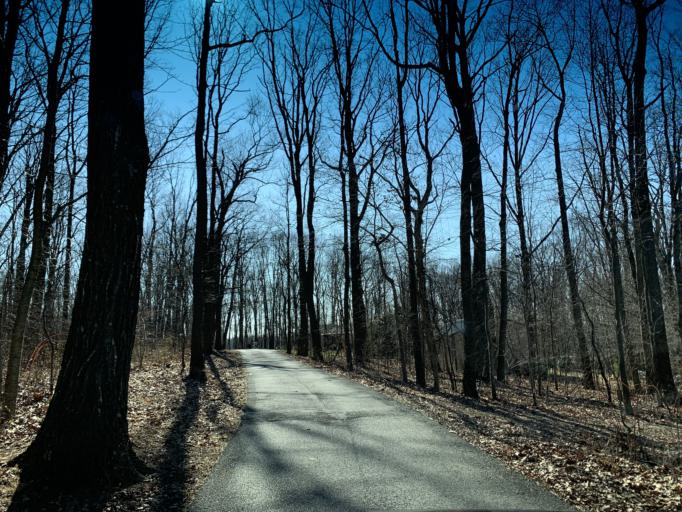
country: US
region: Maryland
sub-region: Carroll County
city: Manchester
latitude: 39.6323
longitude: -76.9192
